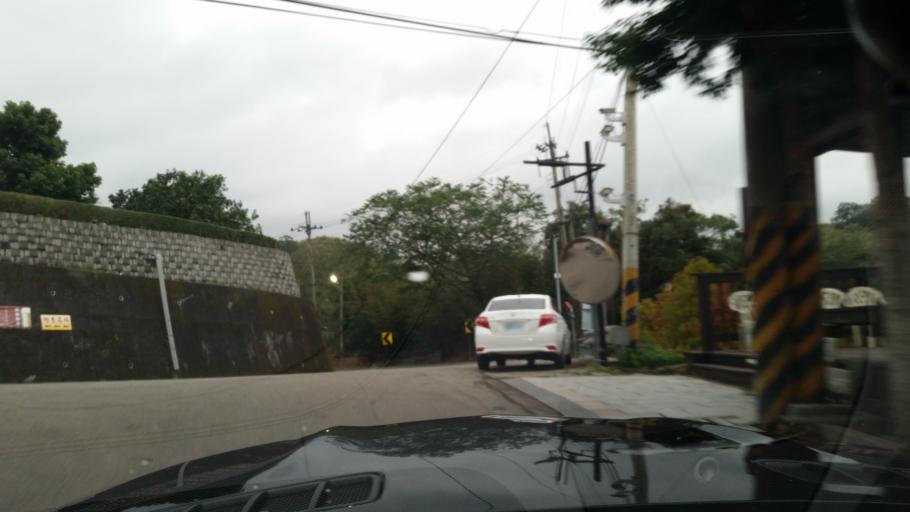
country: TW
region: Taiwan
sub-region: Miaoli
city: Miaoli
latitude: 24.5835
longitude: 120.8973
